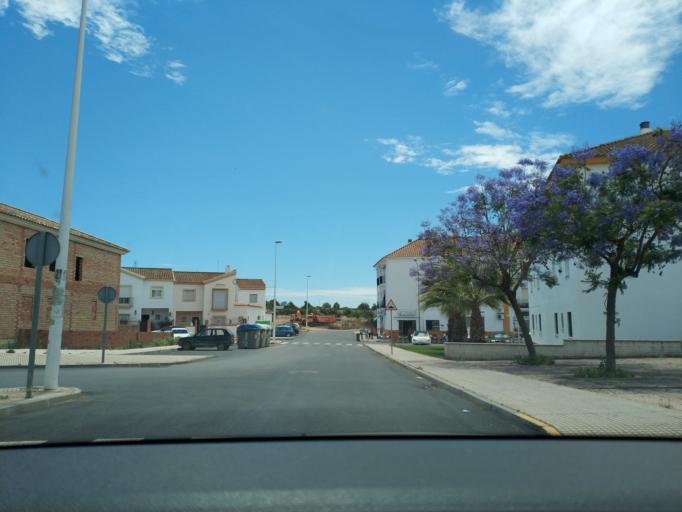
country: ES
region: Andalusia
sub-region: Provincia de Huelva
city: Cartaya
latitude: 37.2842
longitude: -7.1466
